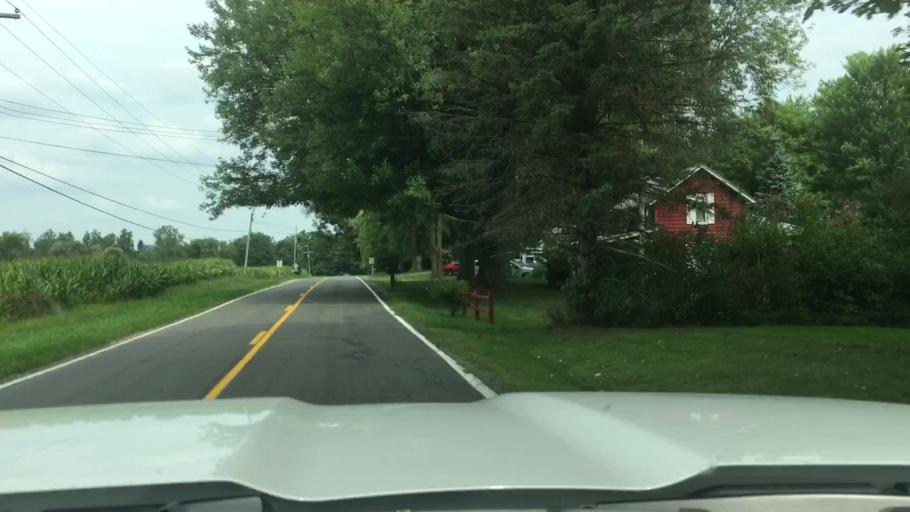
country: US
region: Michigan
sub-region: Ingham County
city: Webberville
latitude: 42.6735
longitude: -84.1890
